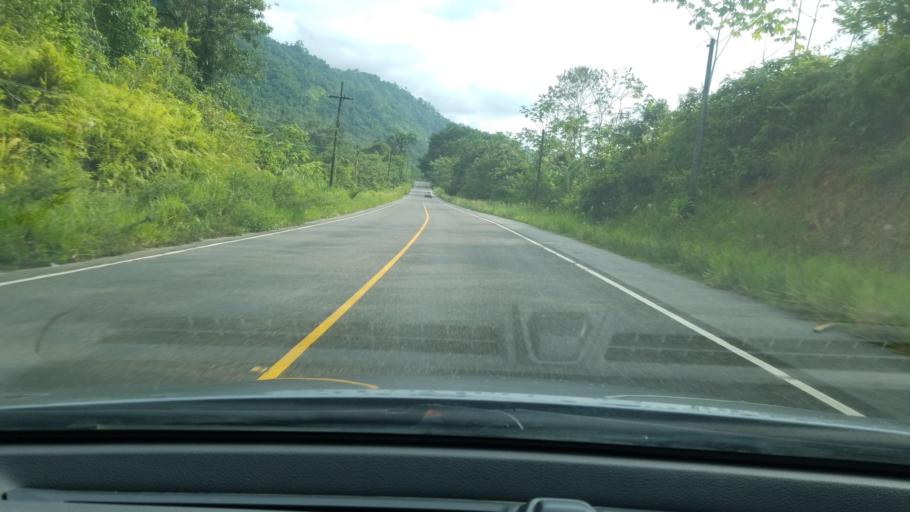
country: HN
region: Cortes
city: Potrerillos
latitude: 15.6028
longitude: -88.2953
